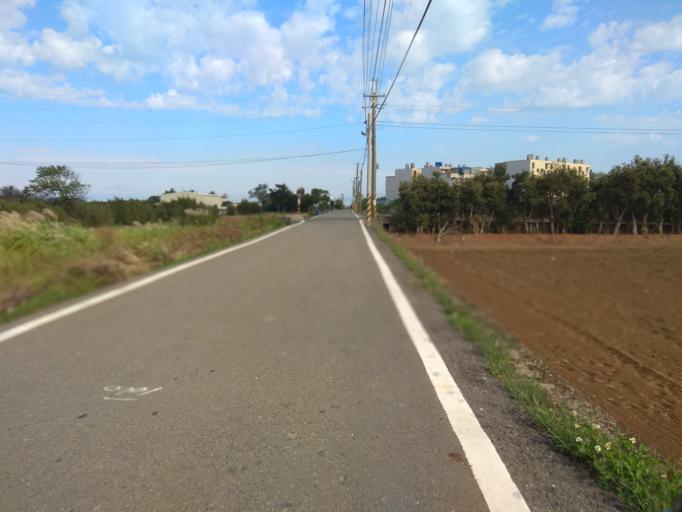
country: TW
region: Taiwan
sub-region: Hsinchu
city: Zhubei
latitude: 24.9898
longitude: 121.0367
